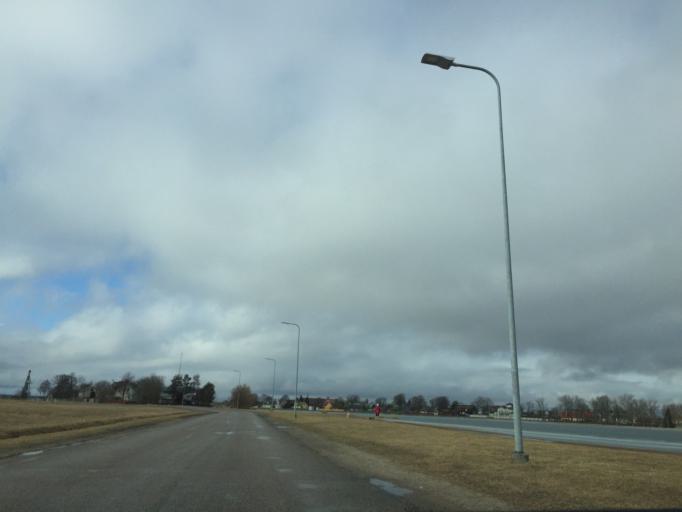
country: EE
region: Laeaene
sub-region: Haapsalu linn
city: Haapsalu
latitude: 58.9505
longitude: 23.5268
